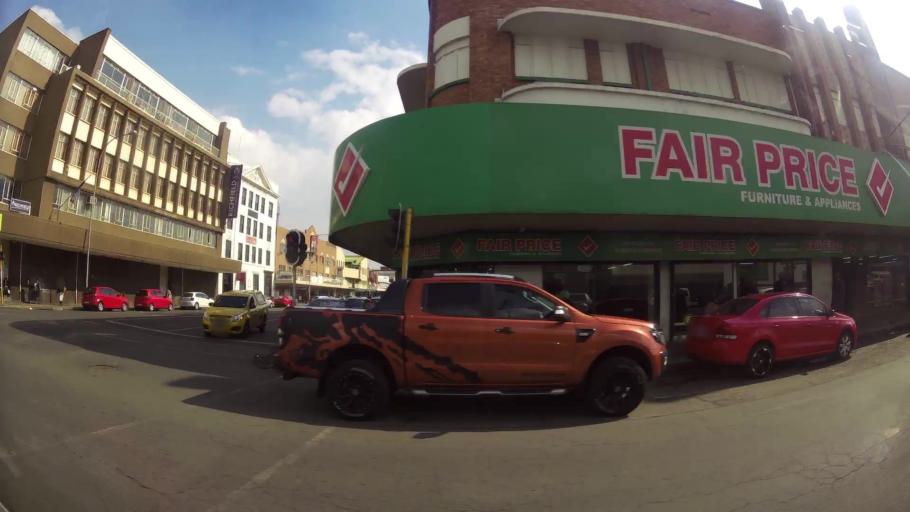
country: ZA
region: Gauteng
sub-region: Sedibeng District Municipality
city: Vereeniging
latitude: -26.6721
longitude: 27.9321
